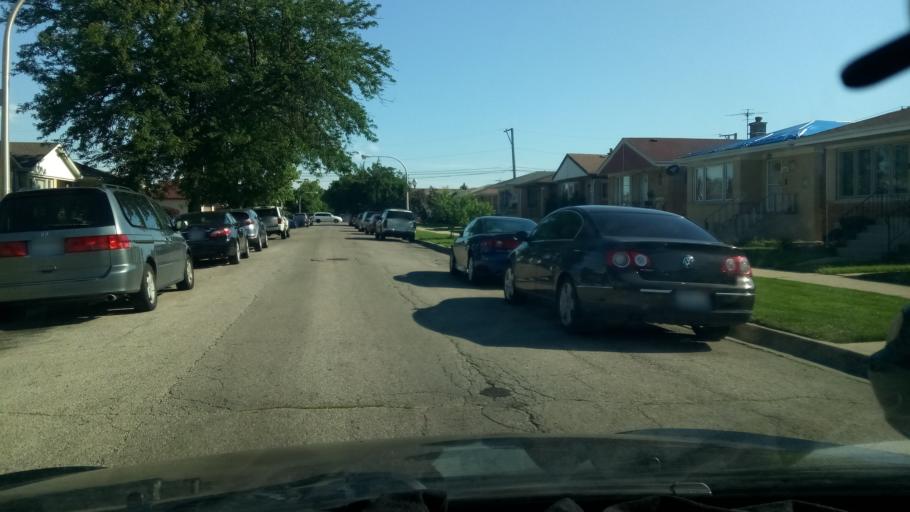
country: US
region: Illinois
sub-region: Cook County
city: Hometown
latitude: 41.7663
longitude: -87.7240
